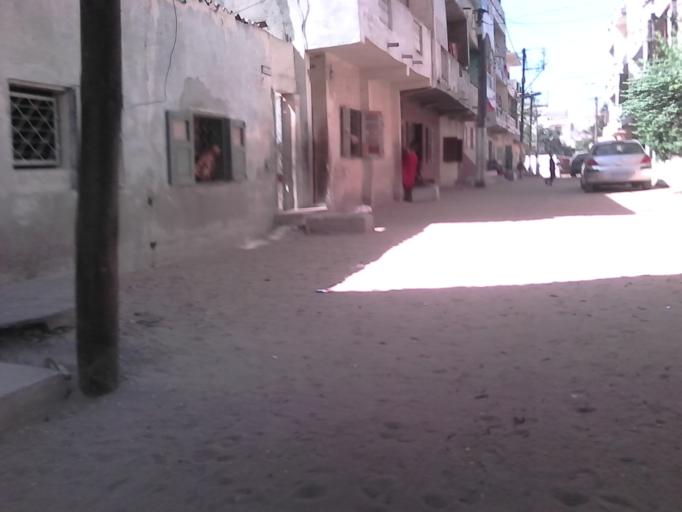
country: SN
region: Dakar
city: Grand Dakar
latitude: 14.7048
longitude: -17.4526
